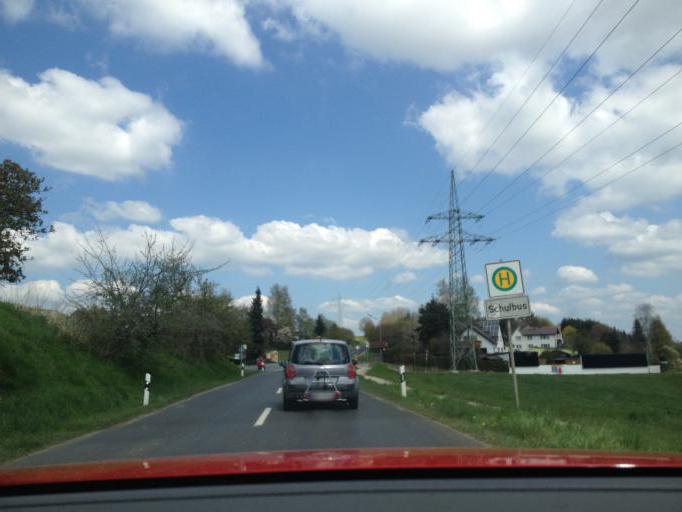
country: DE
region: Bavaria
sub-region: Upper Franconia
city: Marktredwitz
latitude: 50.0107
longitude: 12.1269
